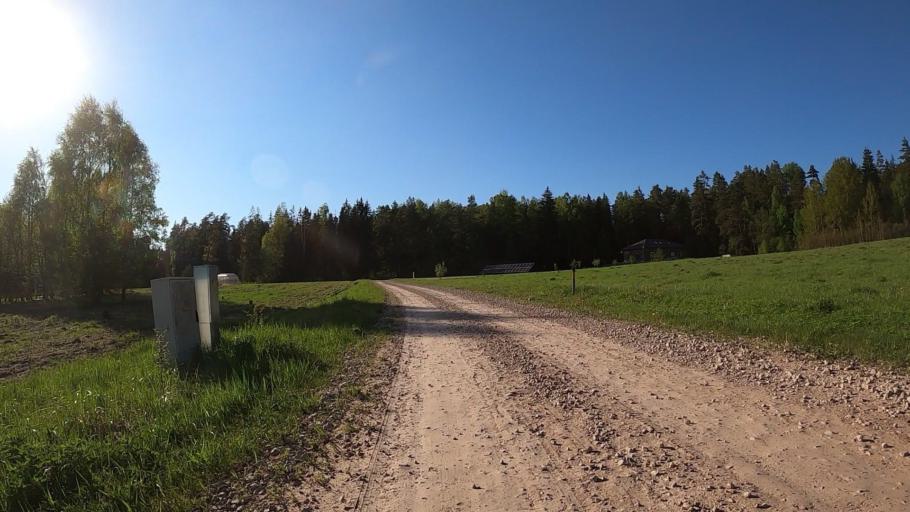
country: LV
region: Baldone
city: Baldone
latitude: 56.7647
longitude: 24.3721
